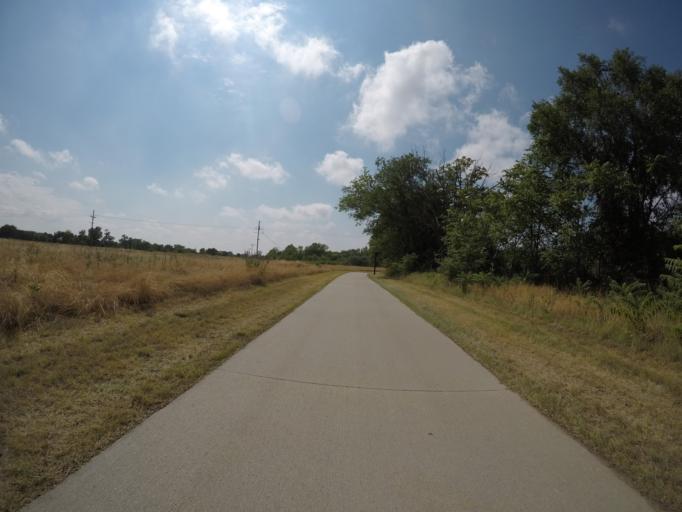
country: US
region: Nebraska
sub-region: Buffalo County
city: Kearney
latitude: 40.6765
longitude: -99.0937
